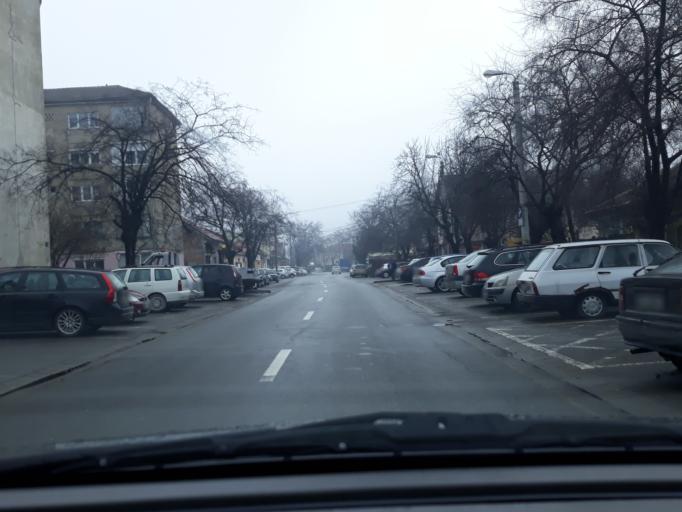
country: RO
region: Bihor
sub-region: Comuna Biharea
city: Oradea
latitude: 47.0435
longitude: 21.9566
